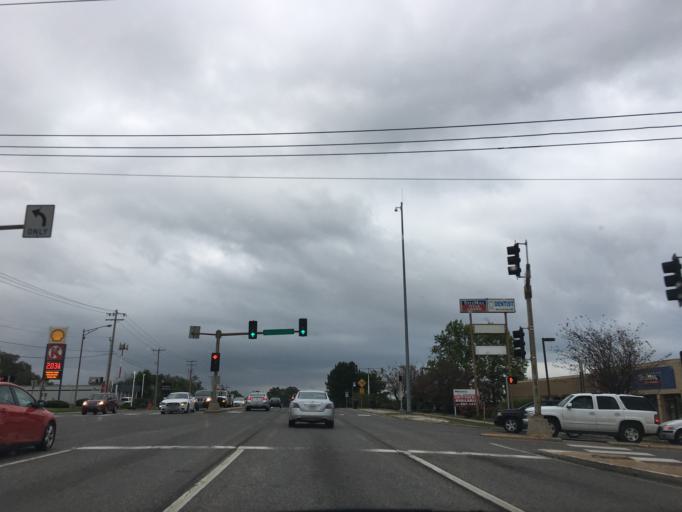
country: US
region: Missouri
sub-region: Saint Louis County
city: Saint Ann
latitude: 38.7310
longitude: -90.4046
